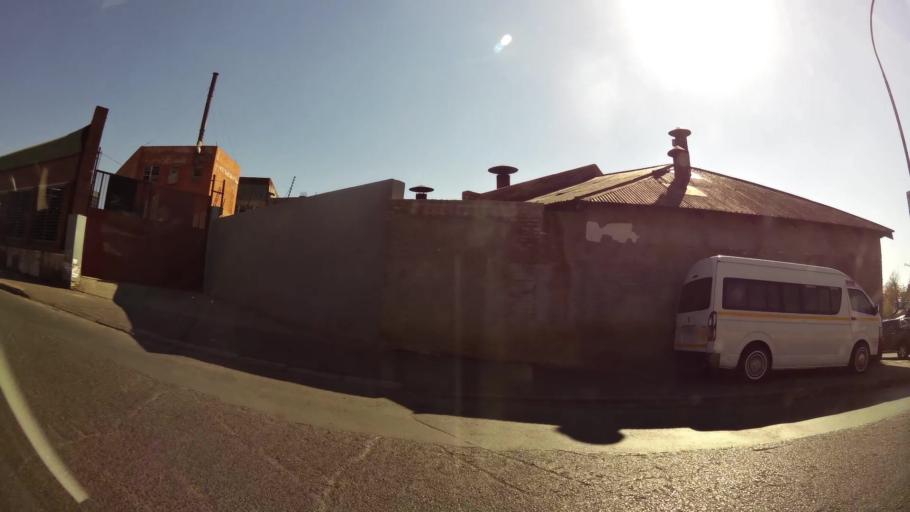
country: ZA
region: Gauteng
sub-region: City of Johannesburg Metropolitan Municipality
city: Johannesburg
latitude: -26.2114
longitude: 28.0470
